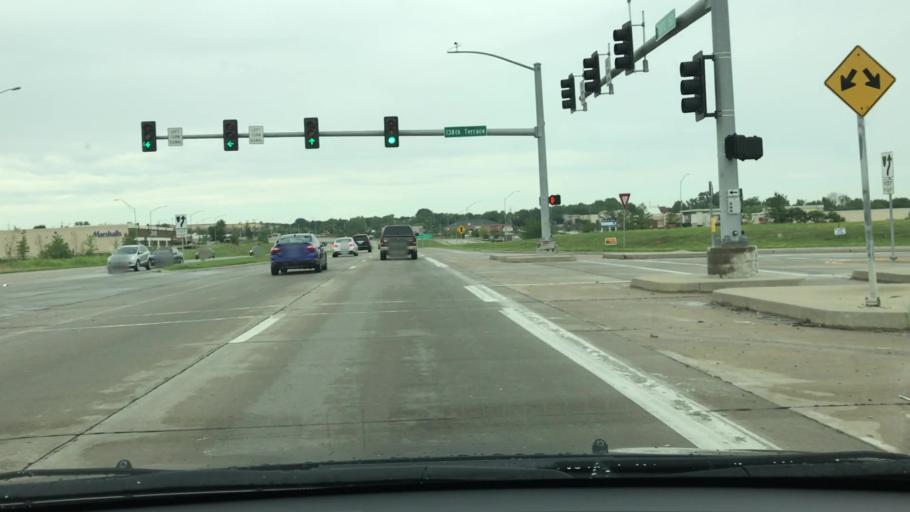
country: US
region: Missouri
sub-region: Jackson County
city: Grandview
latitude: 38.8770
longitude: -94.6033
